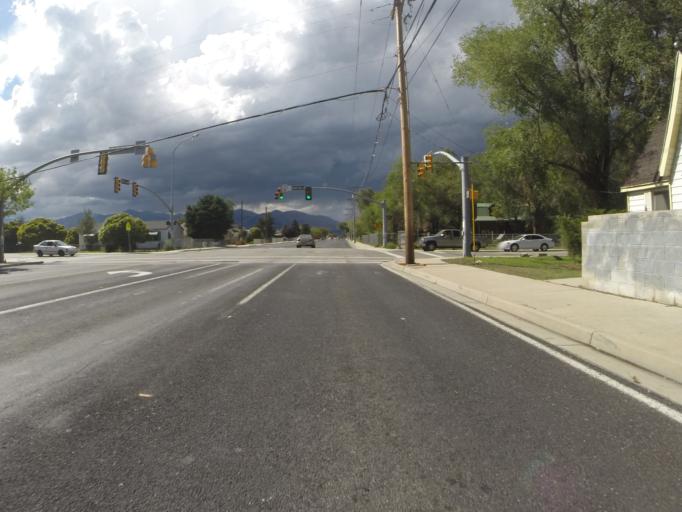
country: US
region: Utah
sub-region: Salt Lake County
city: West Valley City
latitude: 40.7040
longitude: -111.9863
